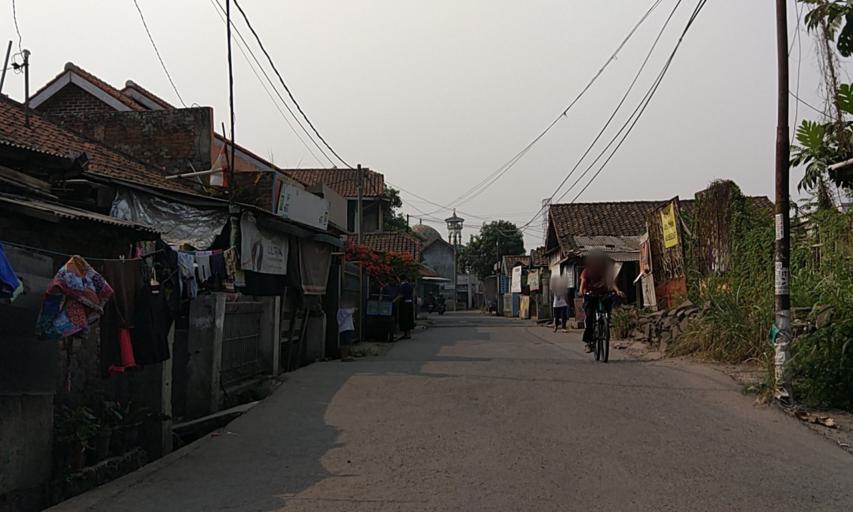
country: ID
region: West Java
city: Margahayukencana
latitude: -6.9682
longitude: 107.5593
